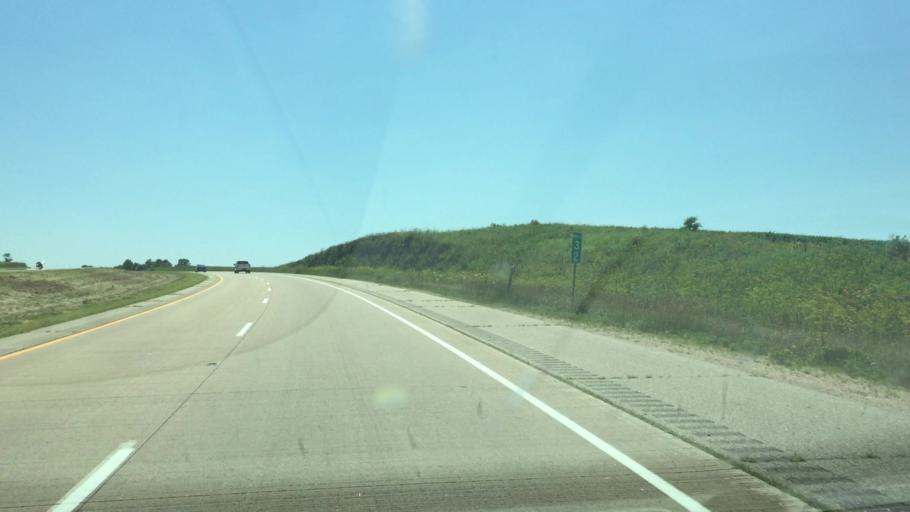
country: US
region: Wisconsin
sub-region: Iowa County
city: Mineral Point
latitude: 42.8074
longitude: -90.2698
